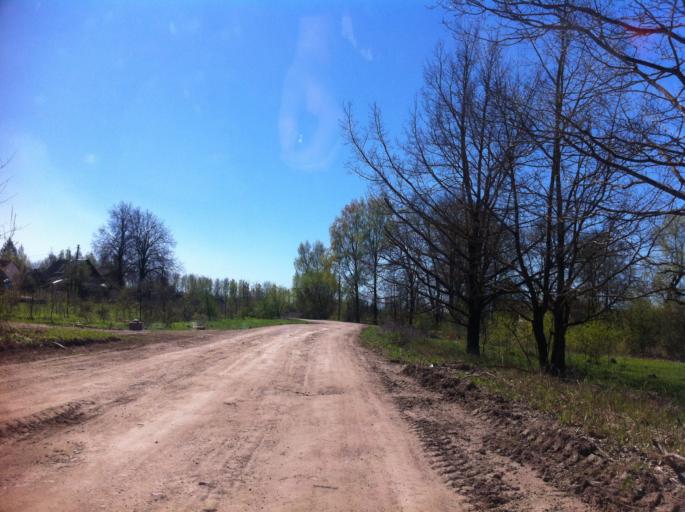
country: RU
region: Pskov
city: Izborsk
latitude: 57.7797
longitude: 27.9627
